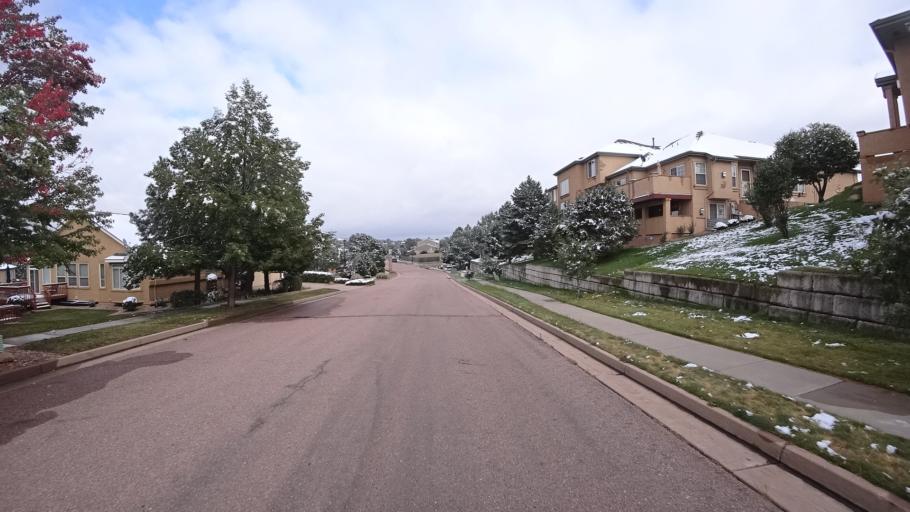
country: US
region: Colorado
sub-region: El Paso County
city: Colorado Springs
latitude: 38.9133
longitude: -104.7950
